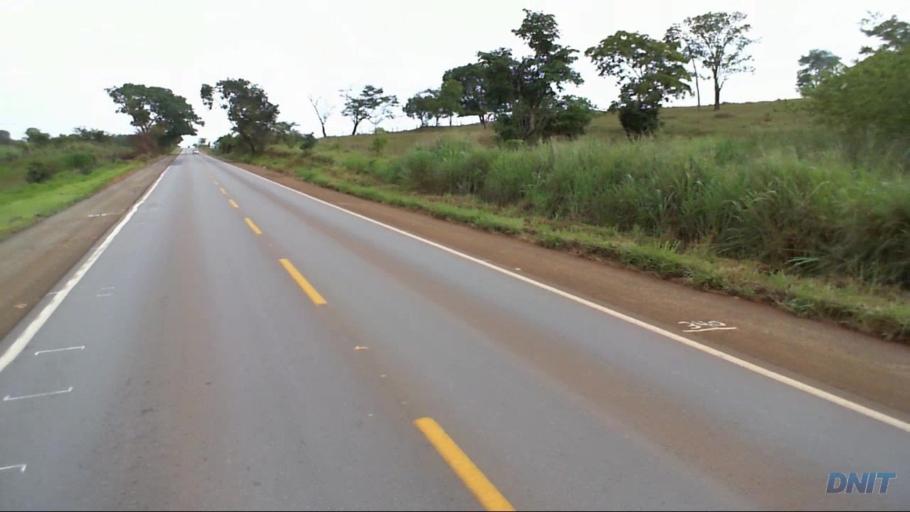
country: BR
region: Goias
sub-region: Uruacu
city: Uruacu
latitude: -14.6835
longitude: -49.1337
